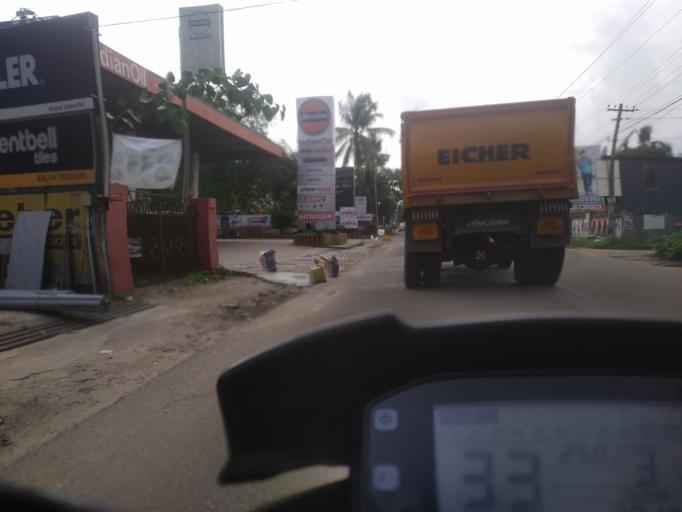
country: IN
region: Kerala
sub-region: Thrissur District
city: Kodungallur
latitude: 10.1429
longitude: 76.2284
